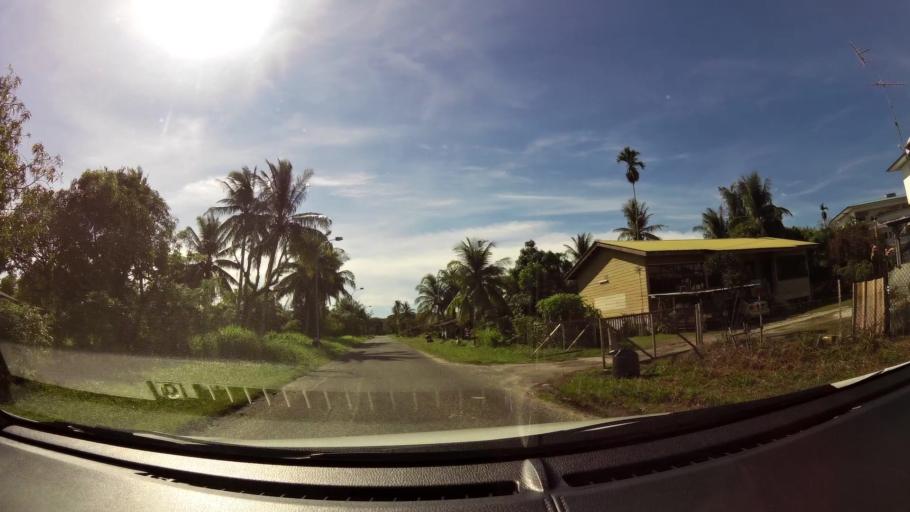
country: BN
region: Belait
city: Kuala Belait
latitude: 4.5792
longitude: 114.2031
